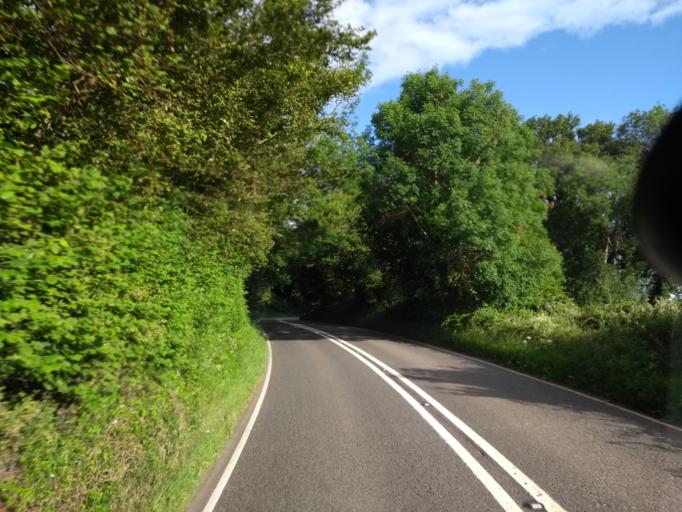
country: GB
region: England
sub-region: Somerset
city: Williton
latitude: 51.1764
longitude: -3.2495
